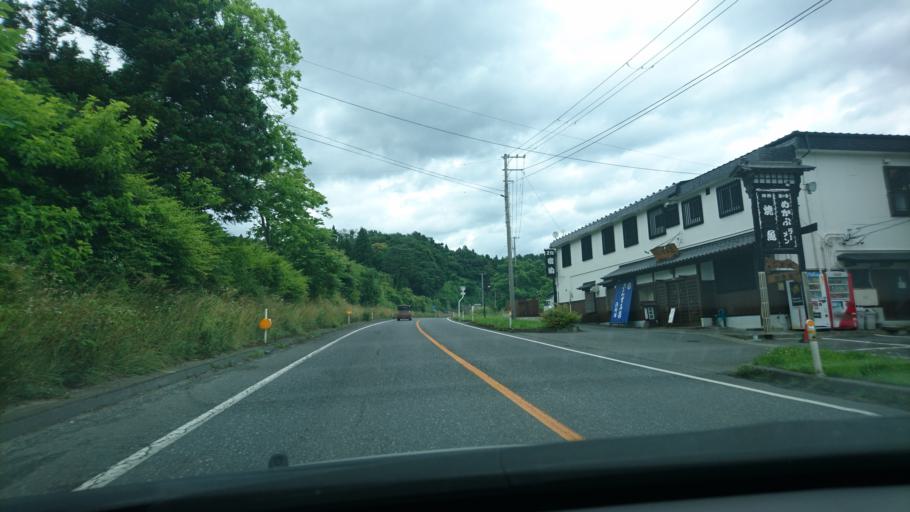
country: JP
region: Iwate
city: Otsuchi
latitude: 39.3860
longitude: 141.9378
